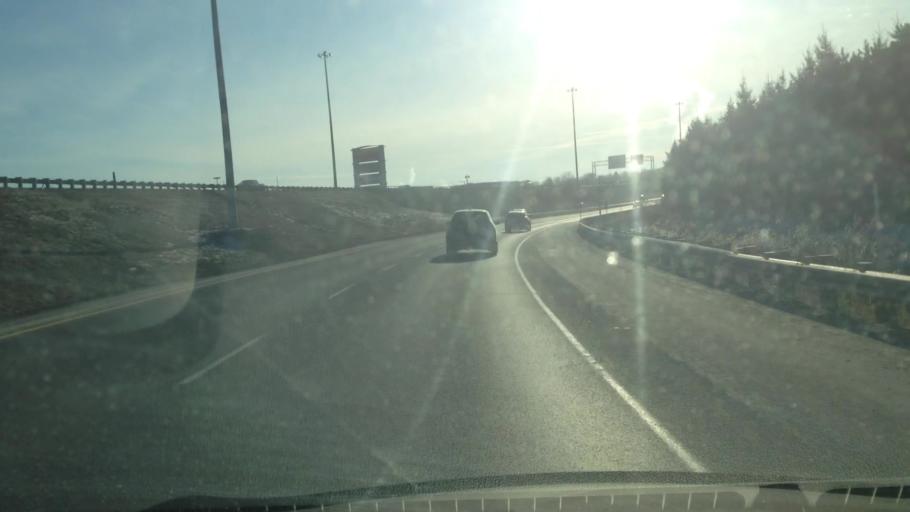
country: CA
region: Quebec
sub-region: Laurentides
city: Saint-Jerome
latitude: 45.7940
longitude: -74.0222
